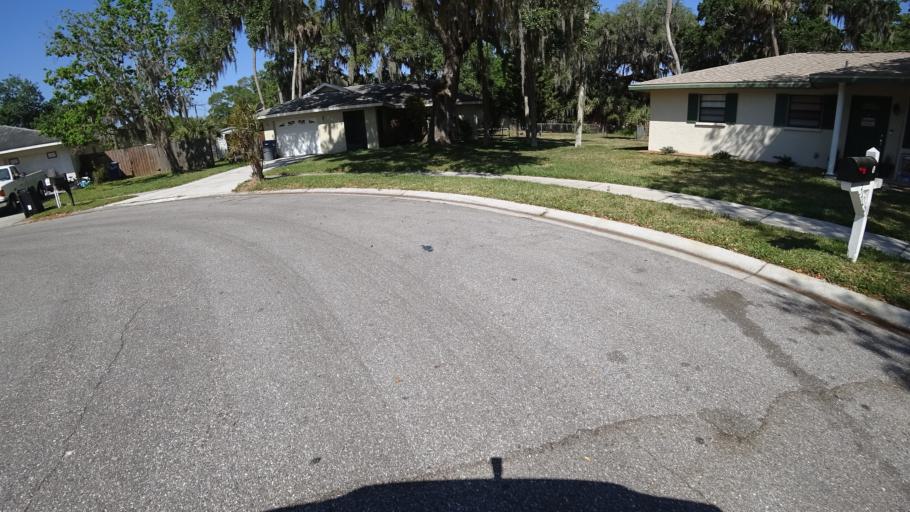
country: US
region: Florida
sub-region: Manatee County
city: Samoset
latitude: 27.4684
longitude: -82.5296
